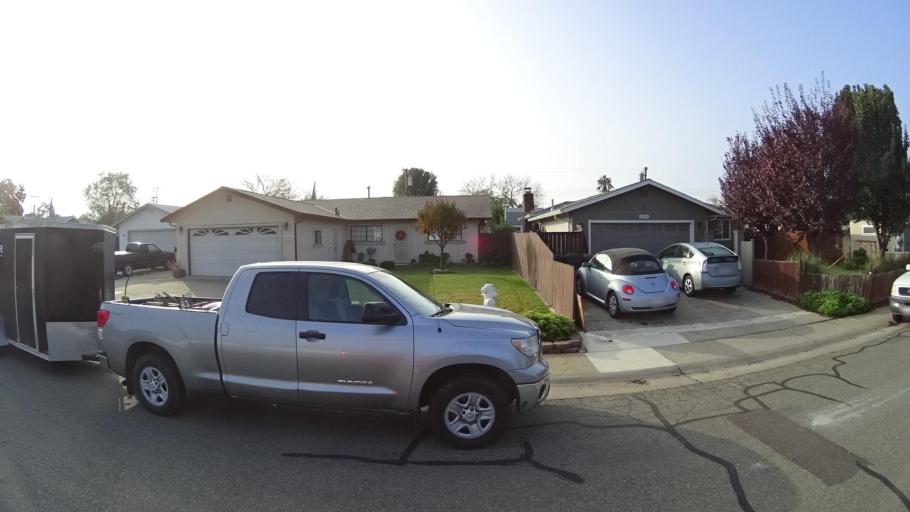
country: US
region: California
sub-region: Sacramento County
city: Elk Grove
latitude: 38.4047
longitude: -121.3550
